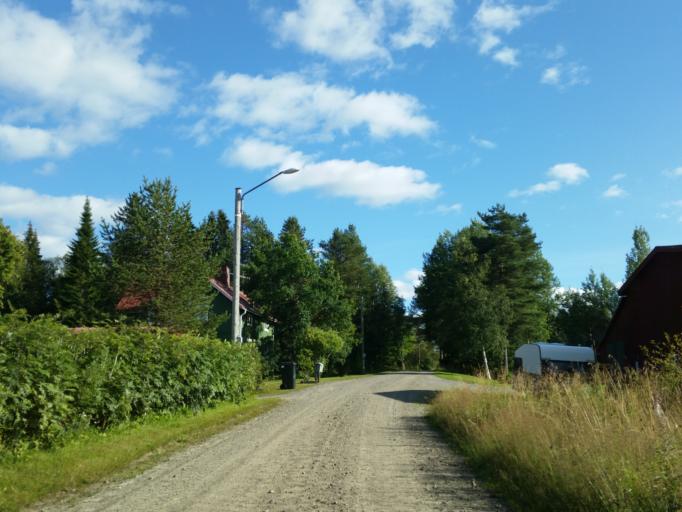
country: SE
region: Vaesterbotten
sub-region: Robertsfors Kommun
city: Robertsfors
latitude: 64.1606
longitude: 20.9562
